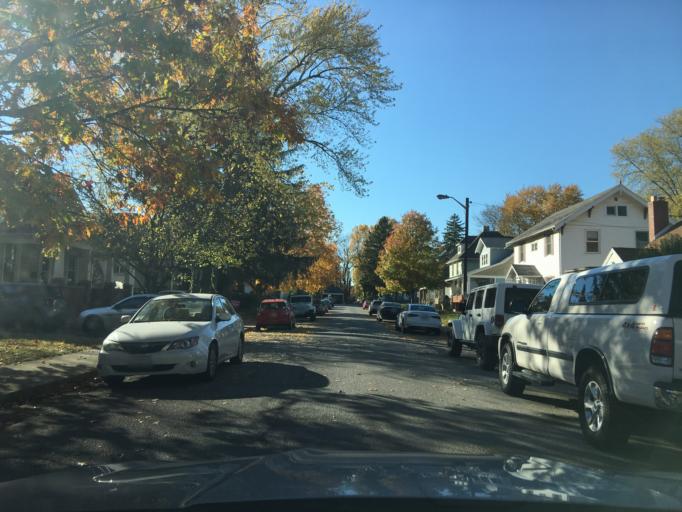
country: US
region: Indiana
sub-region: Tippecanoe County
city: West Lafayette
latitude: 40.4318
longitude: -86.9090
